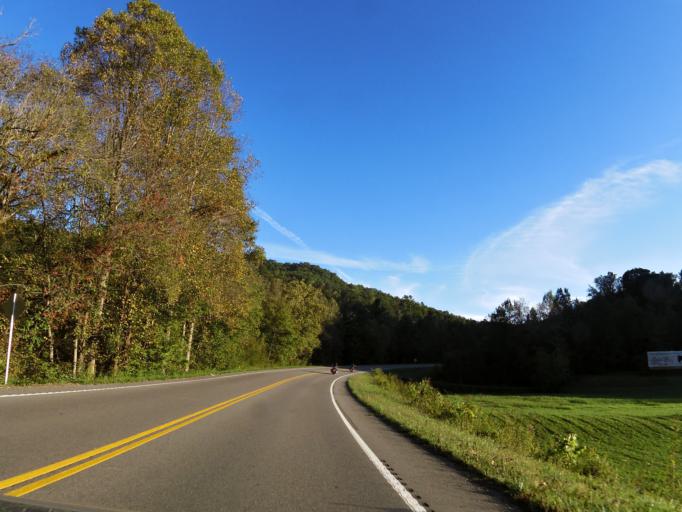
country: US
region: Tennessee
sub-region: Blount County
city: Wildwood
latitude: 35.7114
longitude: -83.8187
